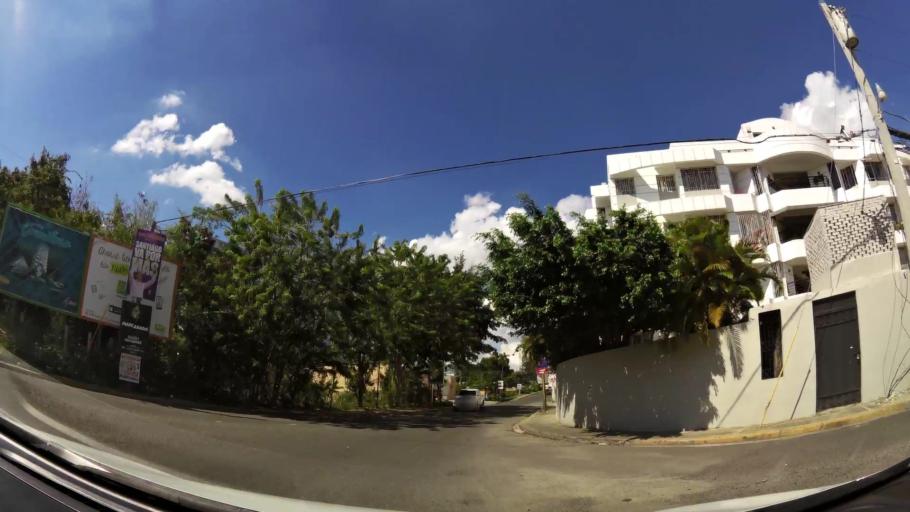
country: DO
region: Santiago
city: Santiago de los Caballeros
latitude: 19.4508
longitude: -70.6847
